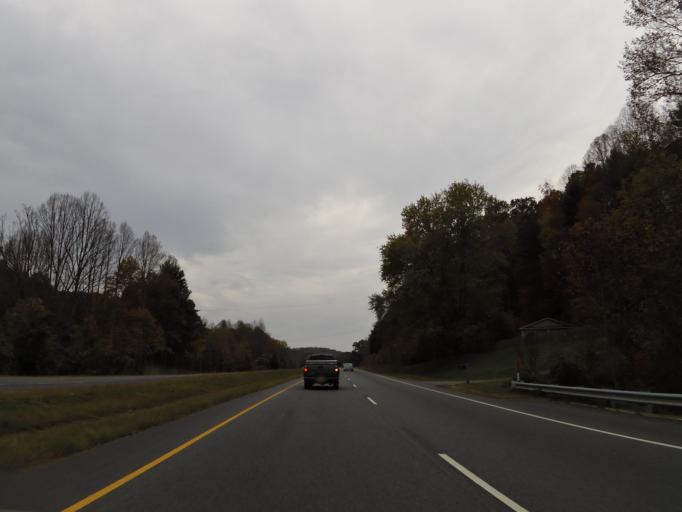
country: US
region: North Carolina
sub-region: Caldwell County
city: Lenoir
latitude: 35.9768
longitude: -81.5647
